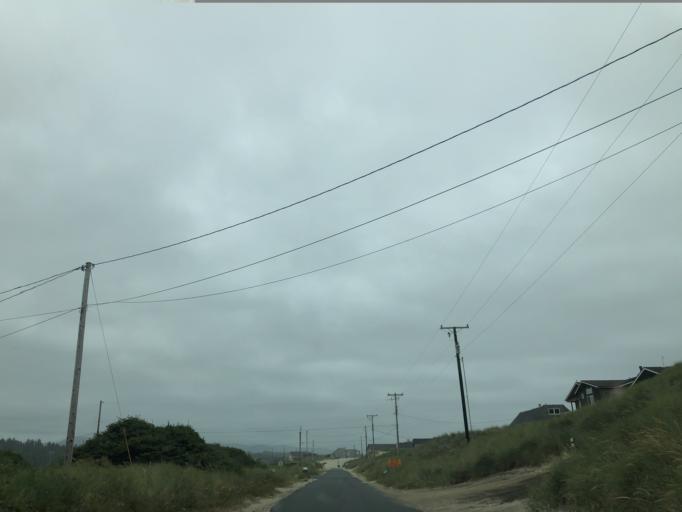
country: US
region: Oregon
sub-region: Lincoln County
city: Waldport
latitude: 44.4316
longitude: -124.0828
